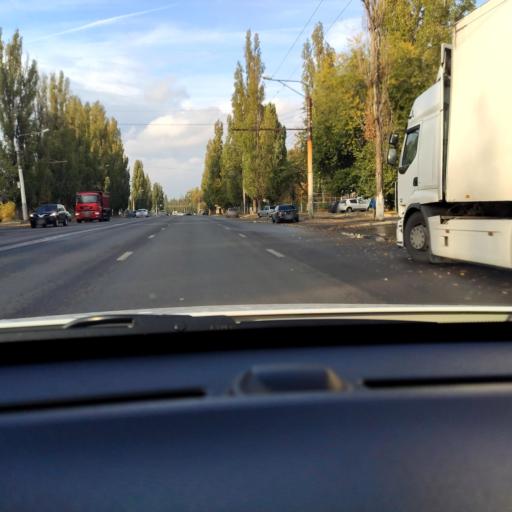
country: RU
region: Voronezj
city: Maslovka
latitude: 51.6136
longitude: 39.2374
